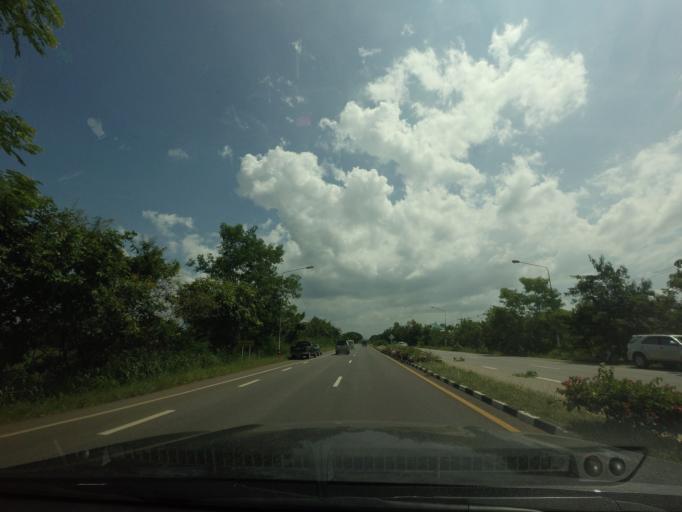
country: TH
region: Phetchabun
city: Phetchabun
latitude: 16.2351
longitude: 101.0813
